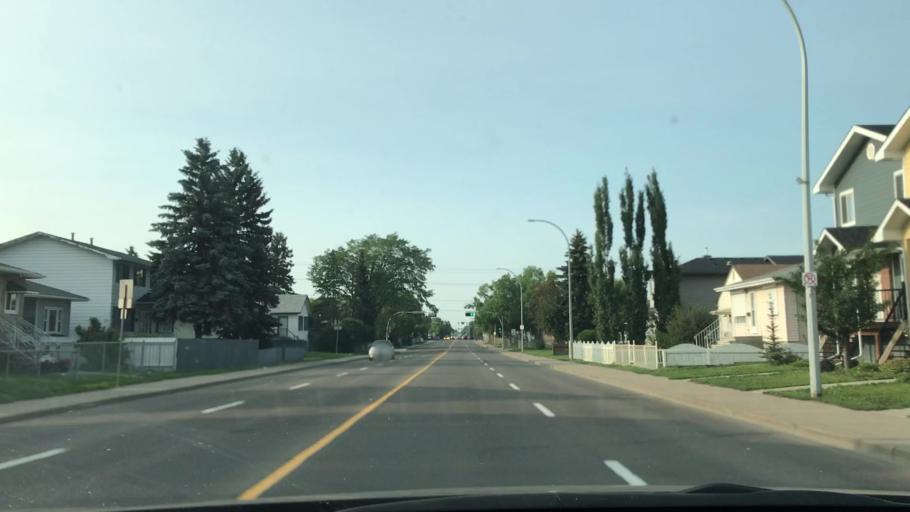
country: CA
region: Alberta
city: Edmonton
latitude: 53.5661
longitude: -113.4673
